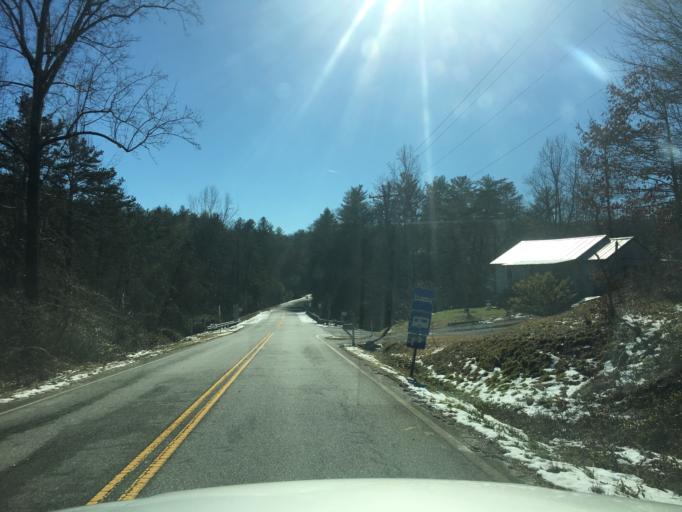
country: US
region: South Carolina
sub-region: Greenville County
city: Slater-Marietta
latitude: 35.0688
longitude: -82.6183
